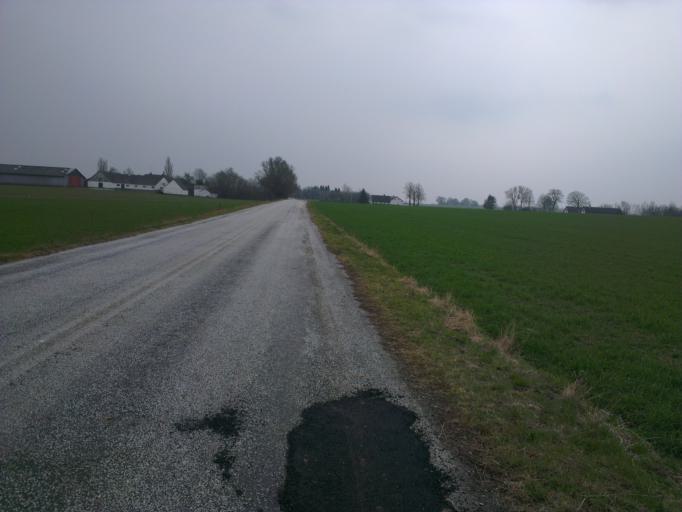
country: DK
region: Capital Region
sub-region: Egedal Kommune
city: Olstykke
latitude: 55.8081
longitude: 12.1088
